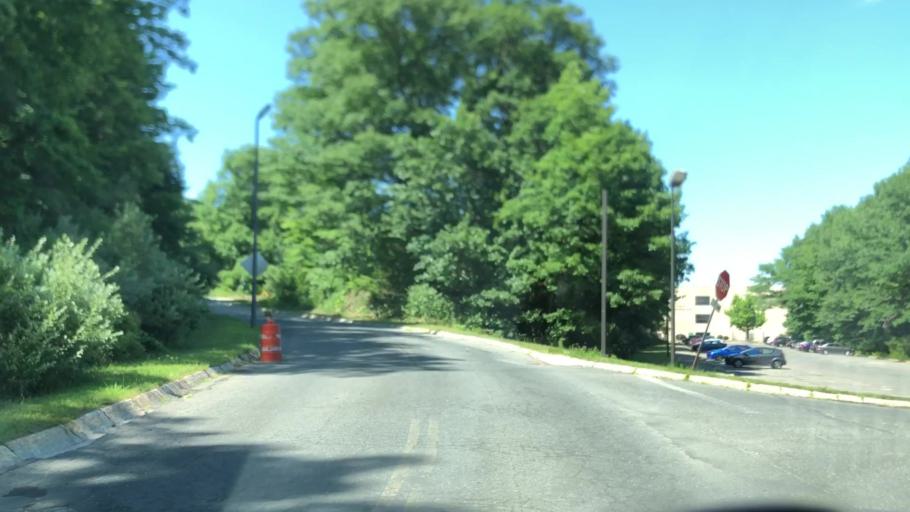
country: US
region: Massachusetts
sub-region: Hampden County
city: Holyoke
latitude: 42.1924
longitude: -72.6532
